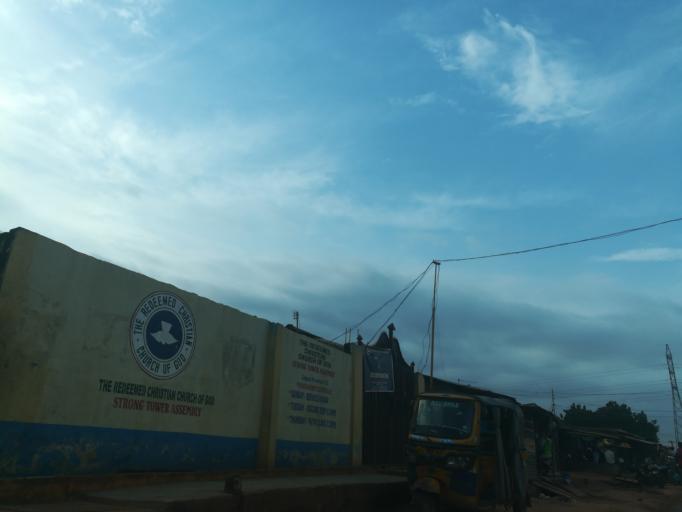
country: NG
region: Lagos
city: Ikorodu
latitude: 6.6243
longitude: 3.5012
